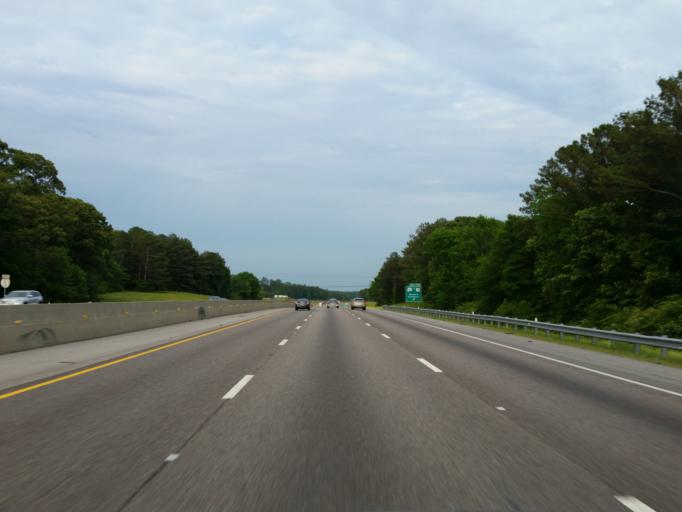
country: US
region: Alabama
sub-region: Calhoun County
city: Bynum
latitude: 33.5829
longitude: -85.9335
